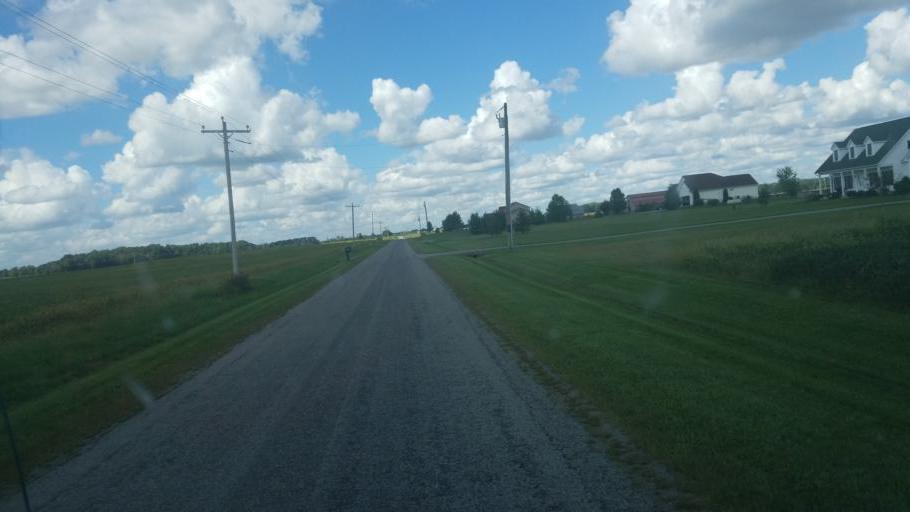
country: US
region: Ohio
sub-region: Union County
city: Richwood
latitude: 40.4555
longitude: -83.4944
